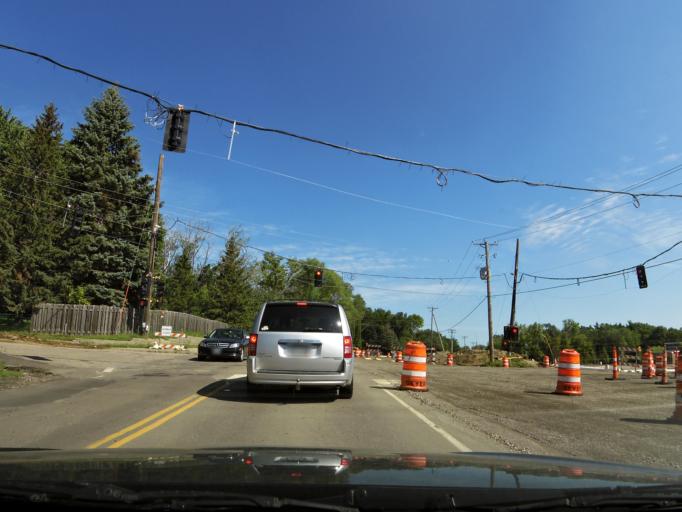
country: US
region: Minnesota
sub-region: Hennepin County
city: Minnetonka
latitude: 44.9009
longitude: -93.5115
